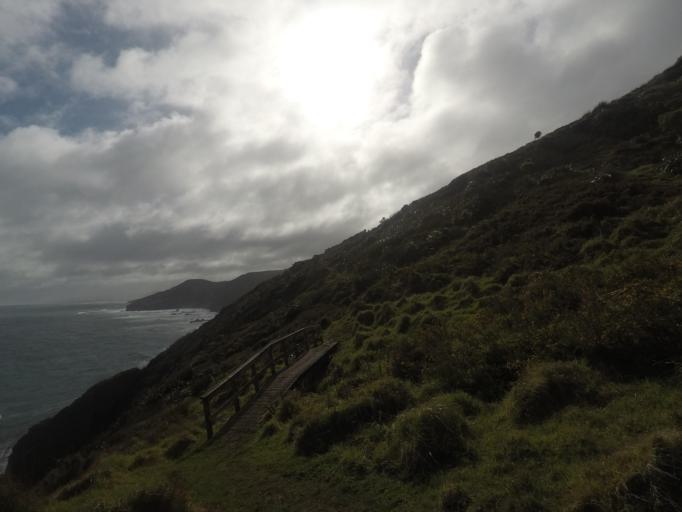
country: NZ
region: Auckland
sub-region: Auckland
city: Muriwai Beach
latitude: -36.8758
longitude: 174.4315
